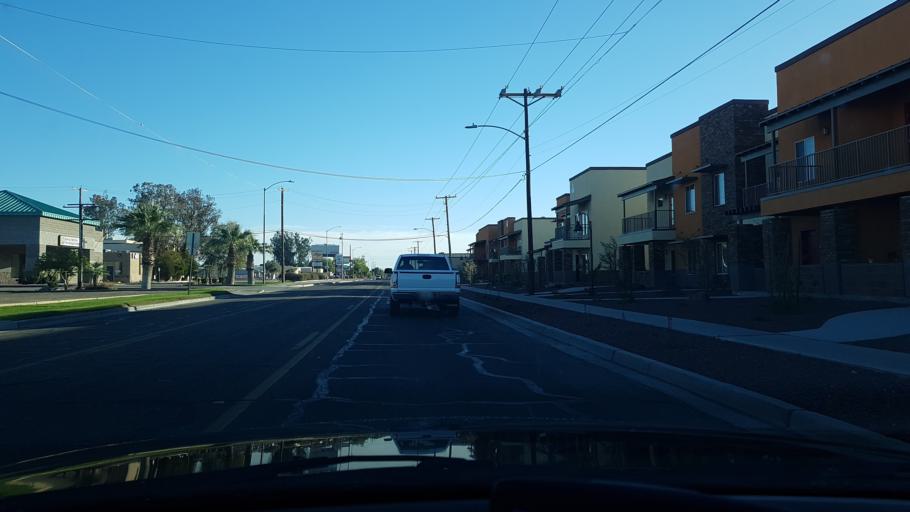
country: US
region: Arizona
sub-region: Yuma County
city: Yuma
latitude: 32.6912
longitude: -114.6160
